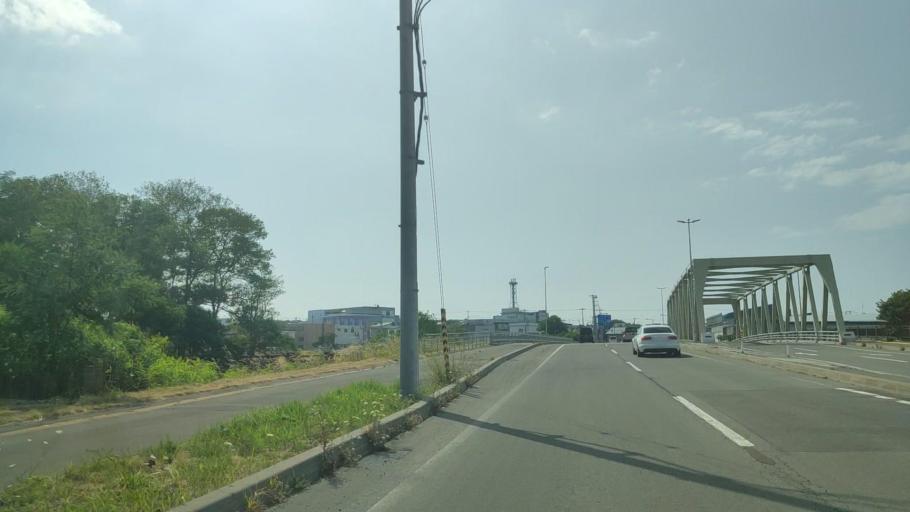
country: JP
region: Hokkaido
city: Rumoi
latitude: 43.9422
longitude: 141.6462
